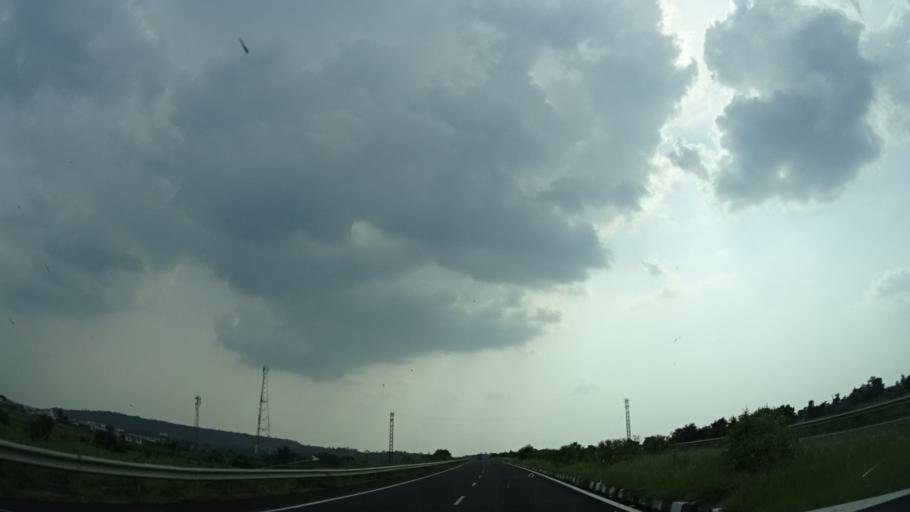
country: IN
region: Telangana
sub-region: Adilabad
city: Nirmal
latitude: 19.1396
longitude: 78.4126
